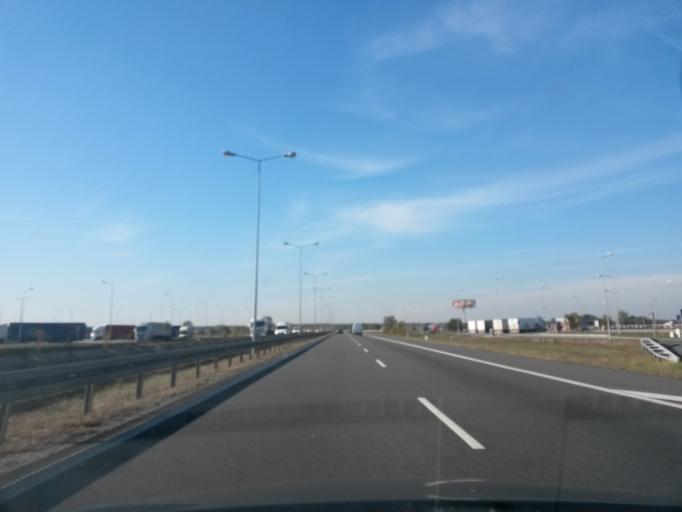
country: PL
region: Opole Voivodeship
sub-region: Powiat opolski
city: Proszkow
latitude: 50.5683
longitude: 17.8622
